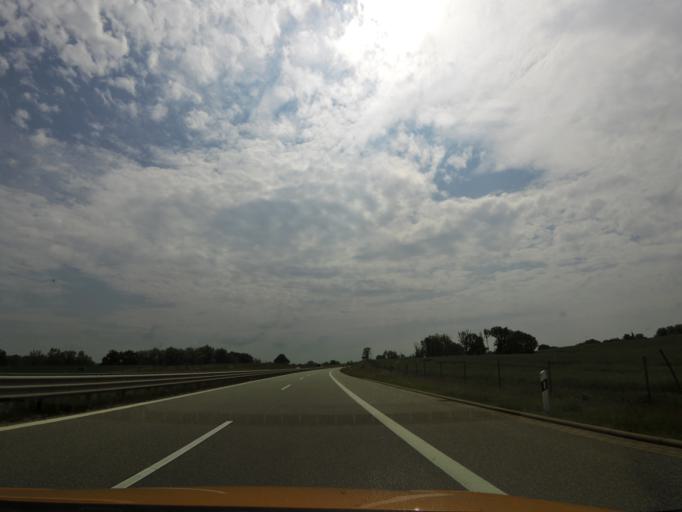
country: DE
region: Mecklenburg-Vorpommern
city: Retgendorf
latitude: 53.7493
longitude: 11.5842
